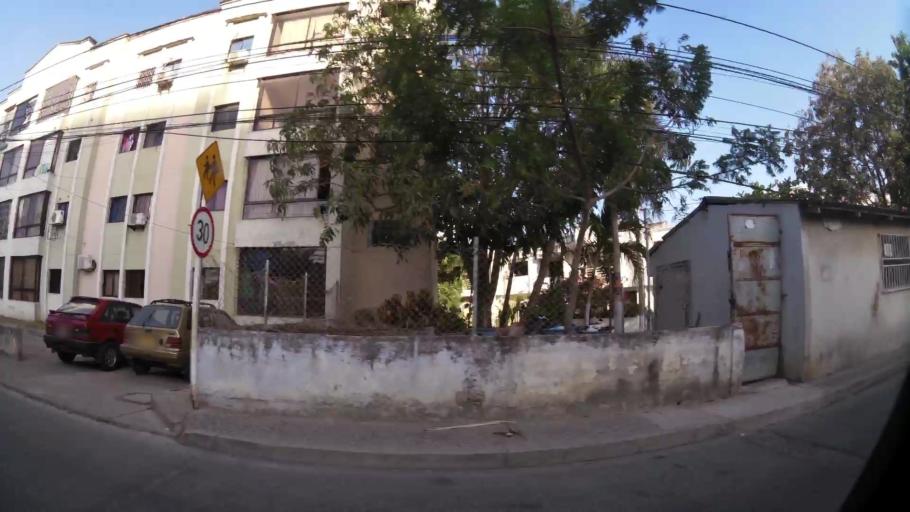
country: CO
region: Bolivar
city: Cartagena
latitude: 10.3972
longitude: -75.4841
